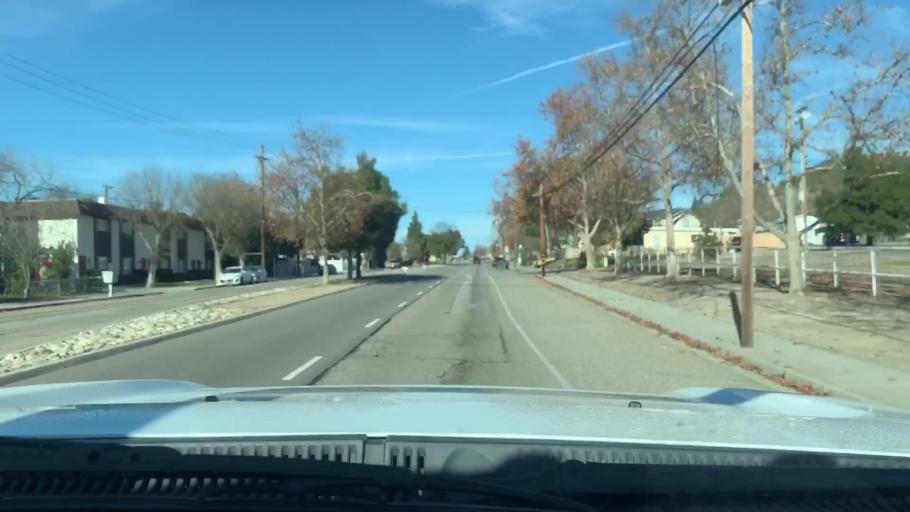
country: US
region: California
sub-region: San Luis Obispo County
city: Atascadero
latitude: 35.4608
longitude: -120.6441
